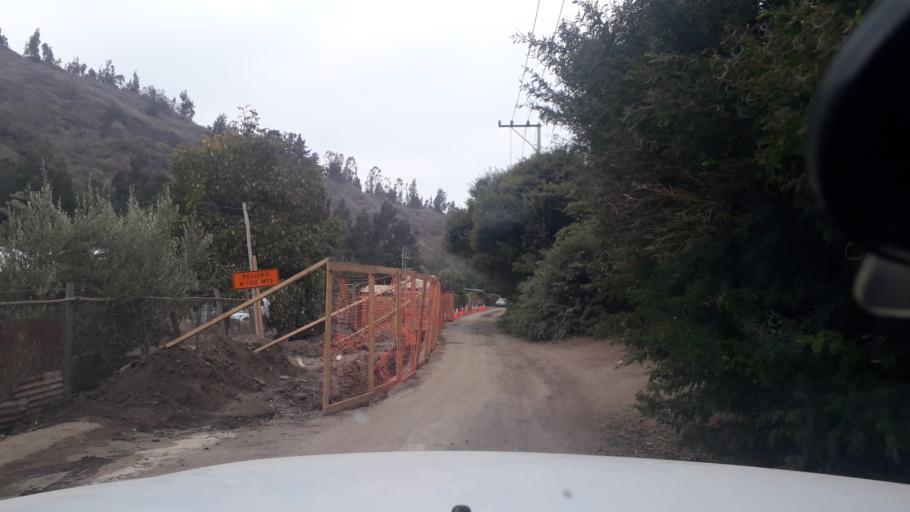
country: CL
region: Valparaiso
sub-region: Provincia de Valparaiso
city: Valparaiso
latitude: -33.1134
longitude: -71.6555
